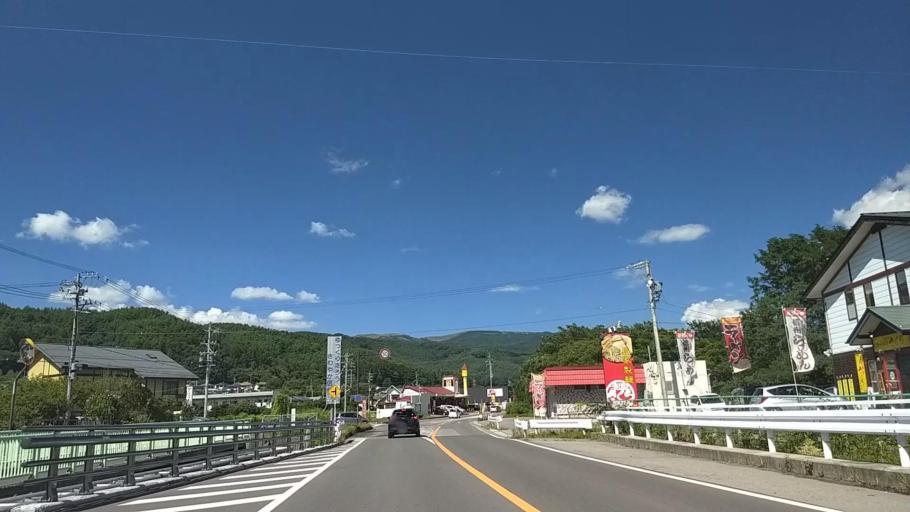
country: JP
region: Nagano
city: Chino
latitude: 36.0207
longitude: 138.1762
